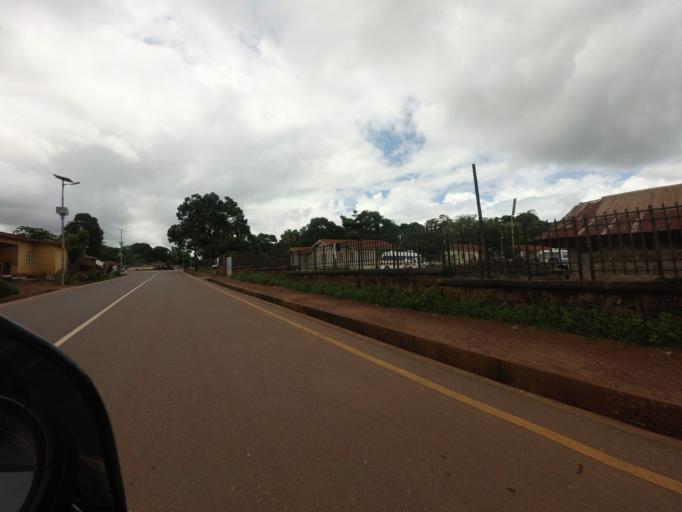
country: SL
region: Northern Province
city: Kambia
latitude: 9.1255
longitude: -12.9132
